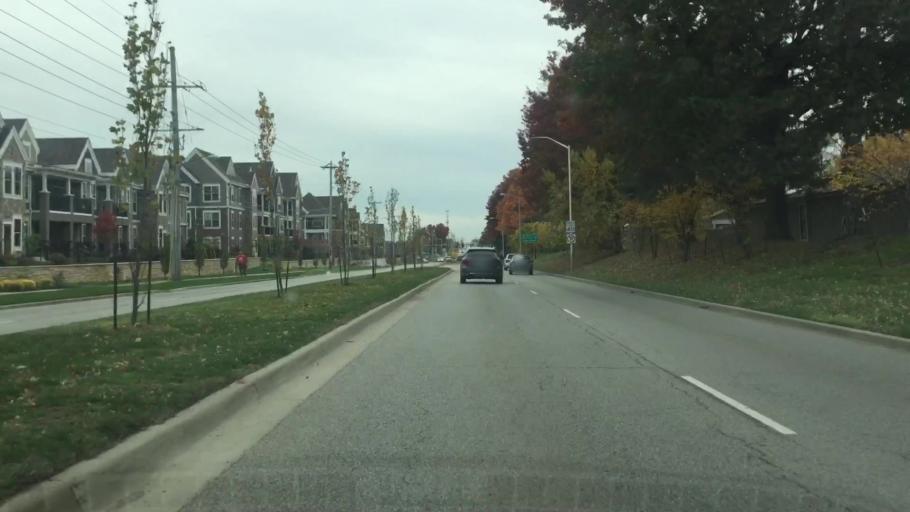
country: US
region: Kansas
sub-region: Johnson County
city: Lenexa
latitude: 38.9813
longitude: -94.7237
